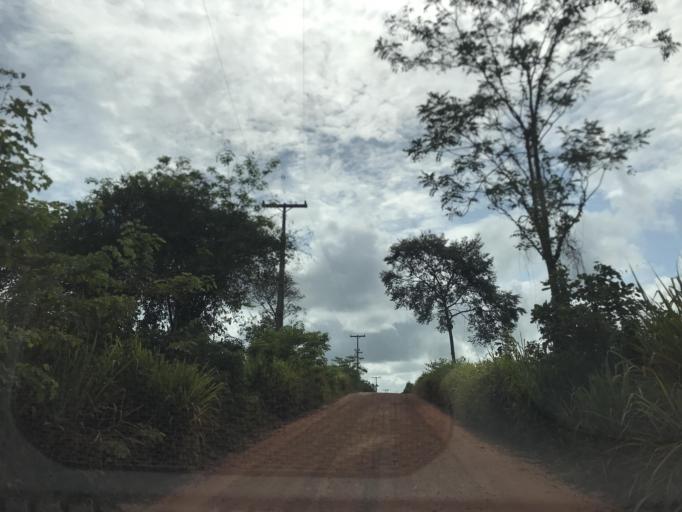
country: BR
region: Bahia
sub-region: Entre Rios
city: Entre Rios
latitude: -12.1653
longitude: -38.1597
